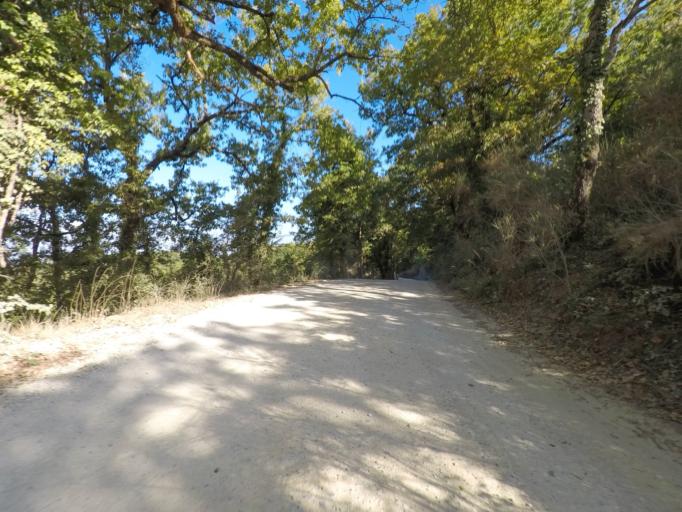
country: IT
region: Tuscany
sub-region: Provincia di Siena
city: Castellina in Chianti
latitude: 43.4300
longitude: 11.3334
